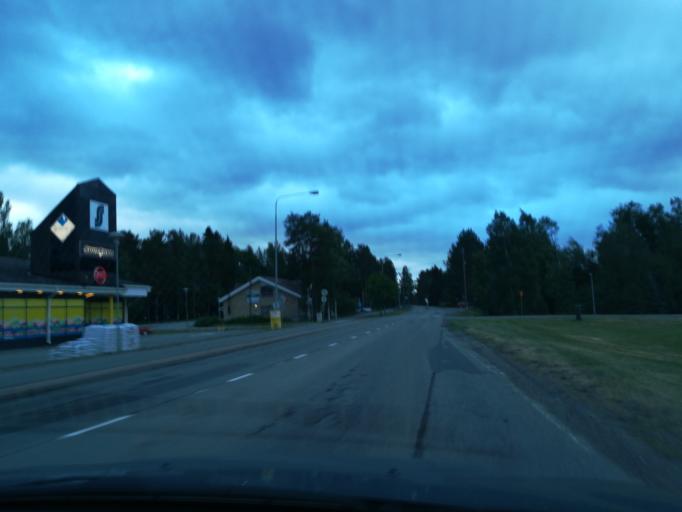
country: FI
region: Southern Savonia
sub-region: Mikkeli
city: Ristiina
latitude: 61.5110
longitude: 27.2468
